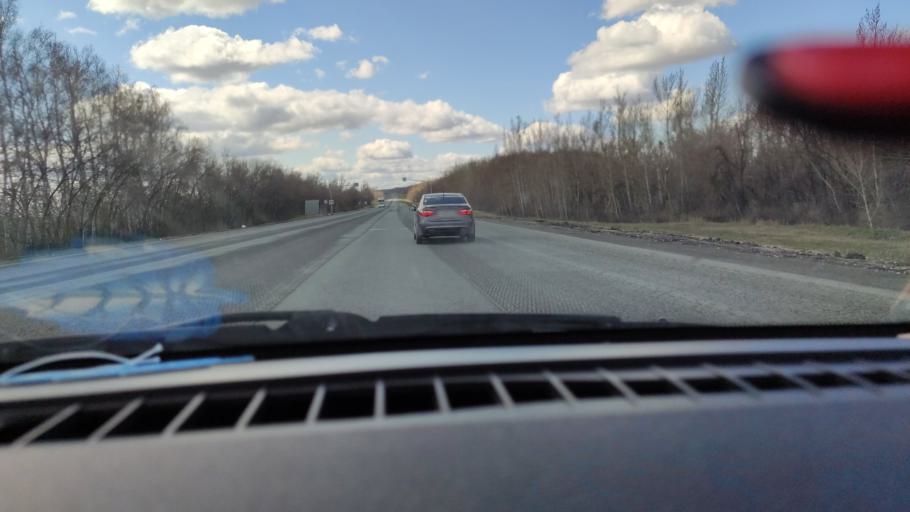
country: RU
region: Saratov
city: Dukhovnitskoye
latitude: 52.6575
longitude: 48.2072
